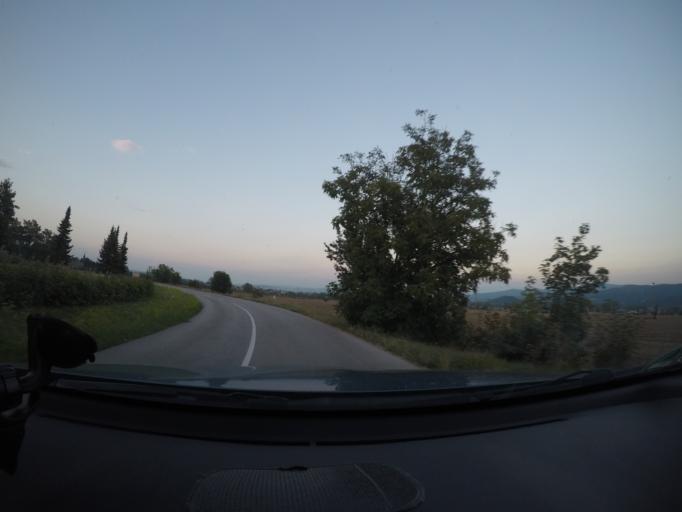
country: SK
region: Trenciansky
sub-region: Okres Nove Mesto nad Vahom
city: Nove Mesto nad Vahom
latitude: 48.8360
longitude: 17.9075
